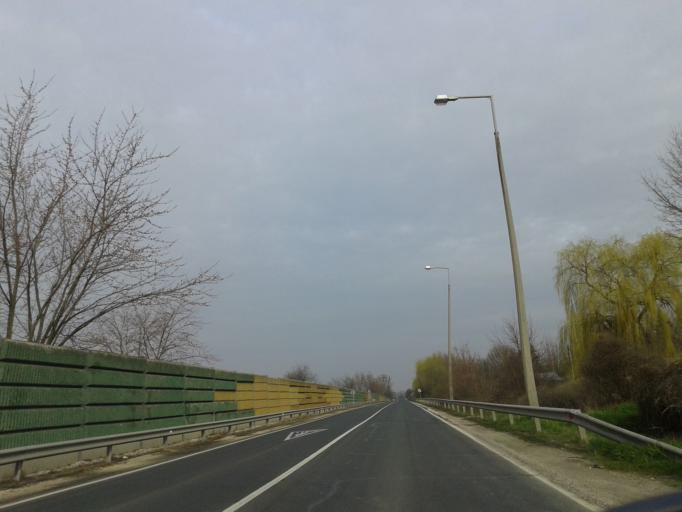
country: HU
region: Komarom-Esztergom
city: Tatabanya
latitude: 47.5827
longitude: 18.4052
